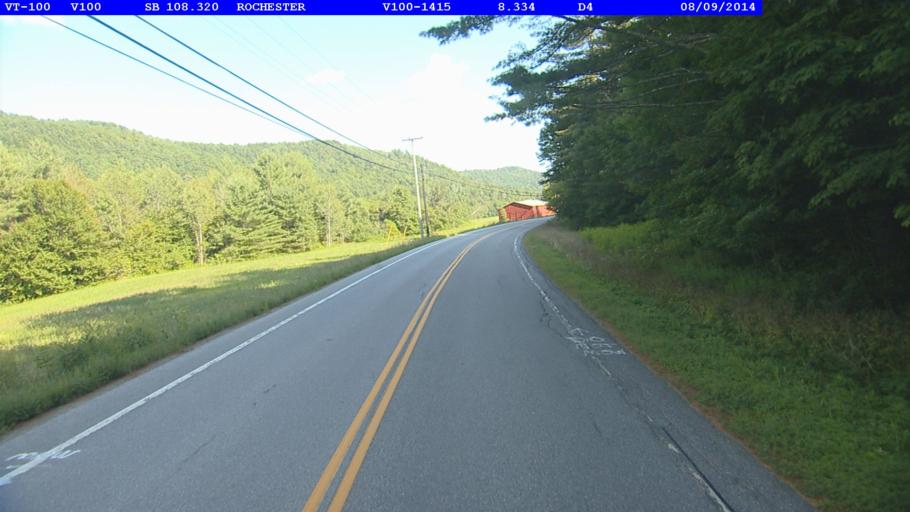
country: US
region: Vermont
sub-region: Orange County
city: Randolph
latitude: 43.9123
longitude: -72.8326
